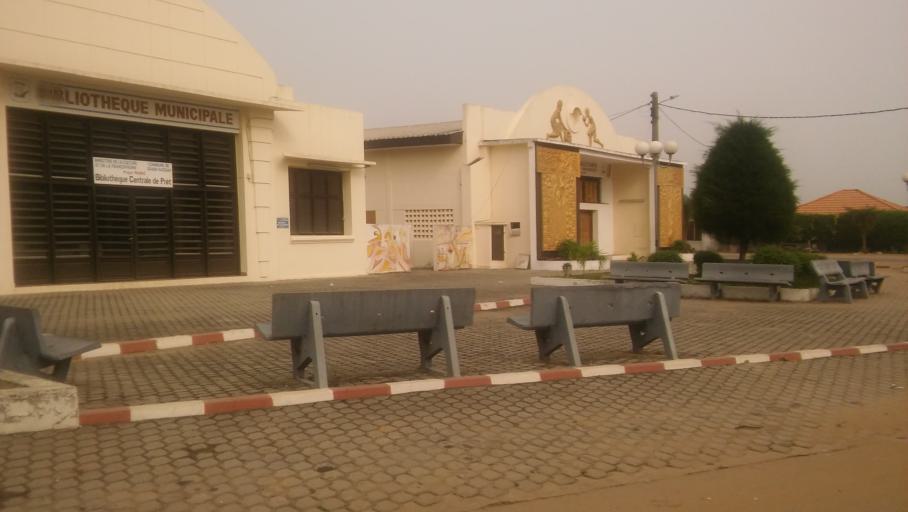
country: CI
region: Sud-Comoe
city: Grand-Bassam
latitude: 5.1958
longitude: -3.7318
